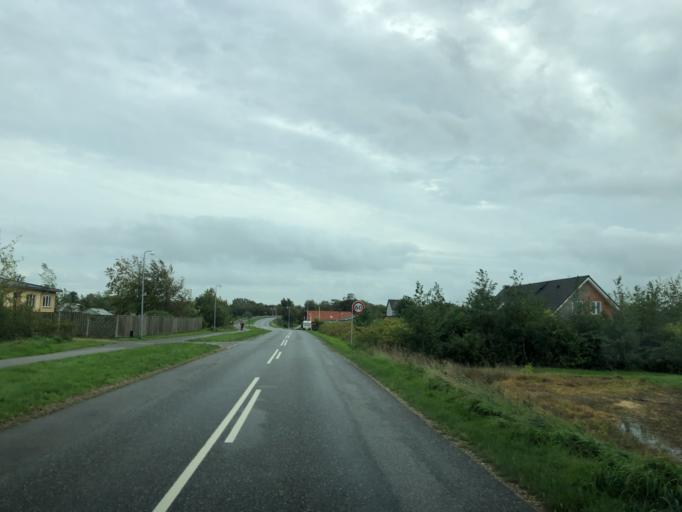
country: DK
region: Central Jutland
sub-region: Herning Kommune
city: Vildbjerg
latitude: 56.1833
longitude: 8.7452
